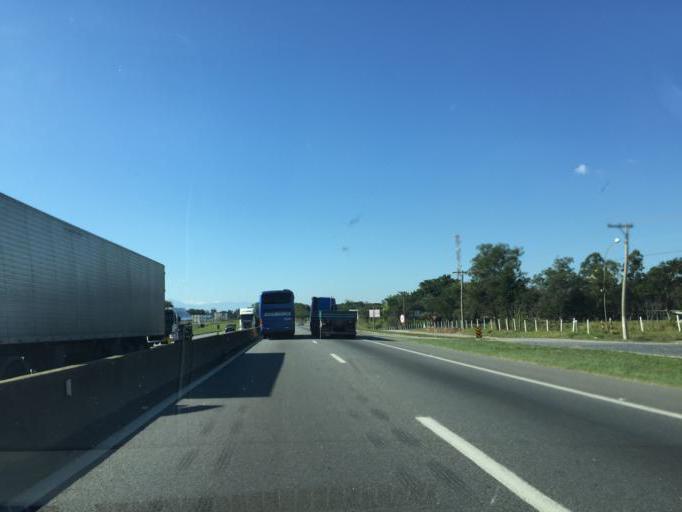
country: BR
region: Sao Paulo
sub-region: Lorena
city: Lorena
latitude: -22.7763
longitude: -45.1406
